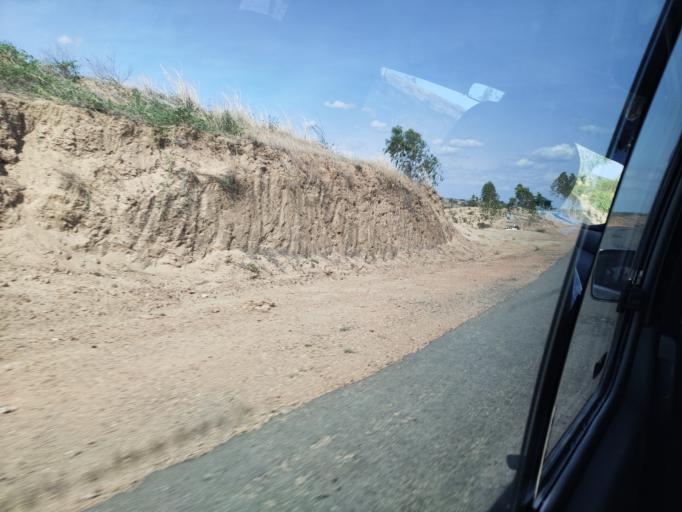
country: MM
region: Magway
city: Yenangyaung
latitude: 20.4713
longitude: 94.9203
